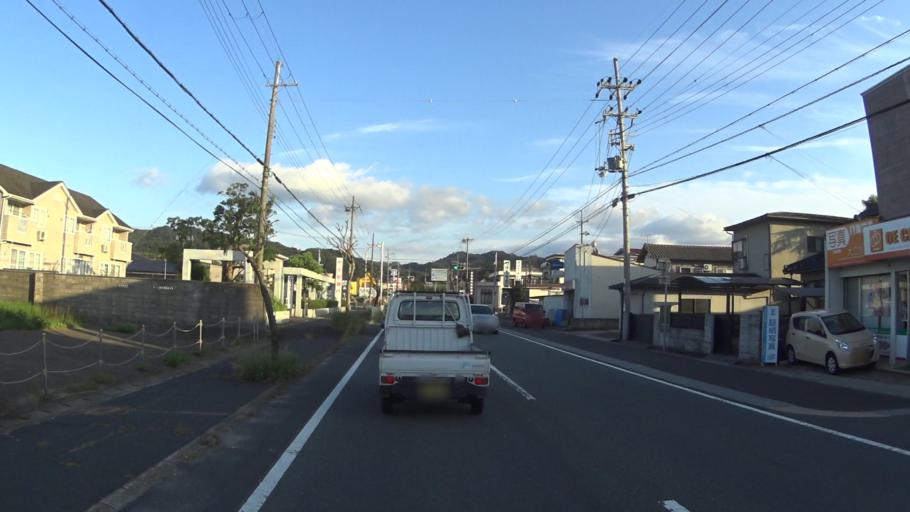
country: JP
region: Kyoto
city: Miyazu
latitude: 35.5852
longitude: 135.0983
